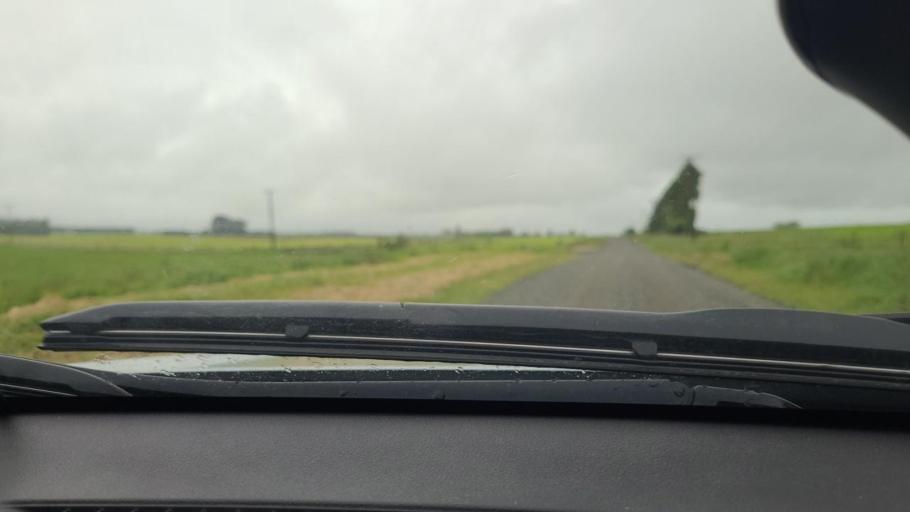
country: NZ
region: Southland
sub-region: Southland District
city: Riverton
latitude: -46.1938
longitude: 168.1041
